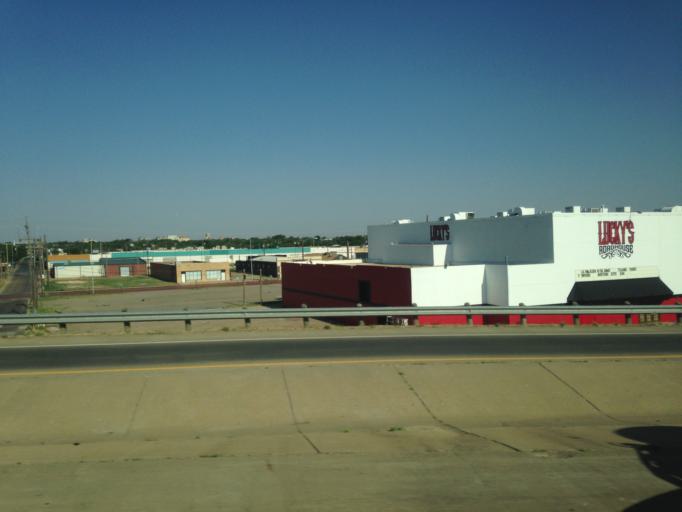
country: US
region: Texas
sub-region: Lubbock County
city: Lubbock
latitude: 33.5744
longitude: -101.8426
